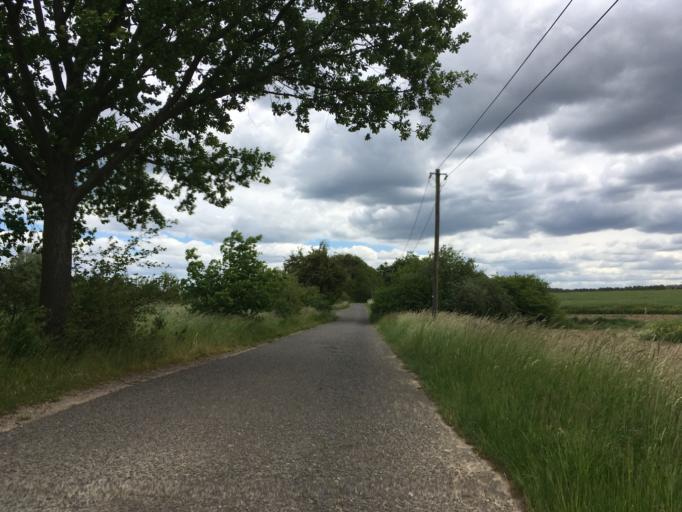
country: DE
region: Brandenburg
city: Hohenfinow
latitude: 52.7670
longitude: 13.9009
